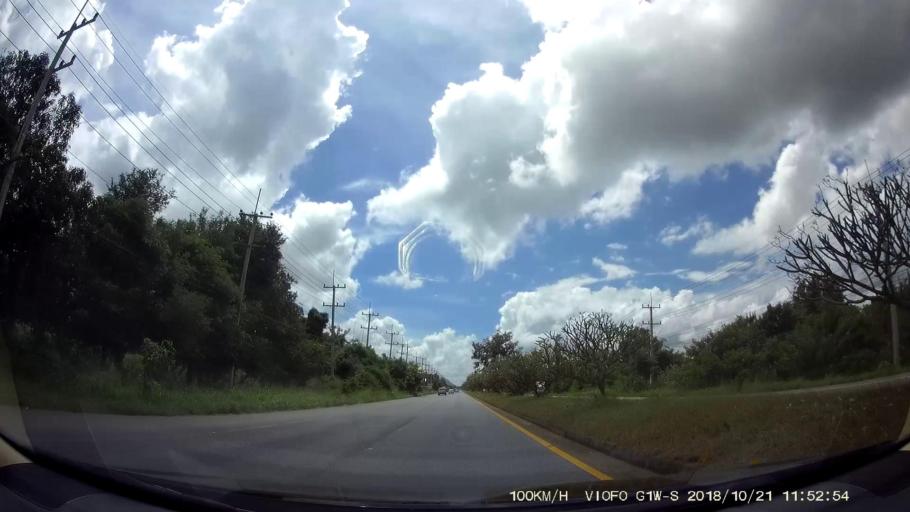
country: TH
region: Chaiyaphum
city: Chatturat
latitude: 15.6029
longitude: 101.9090
